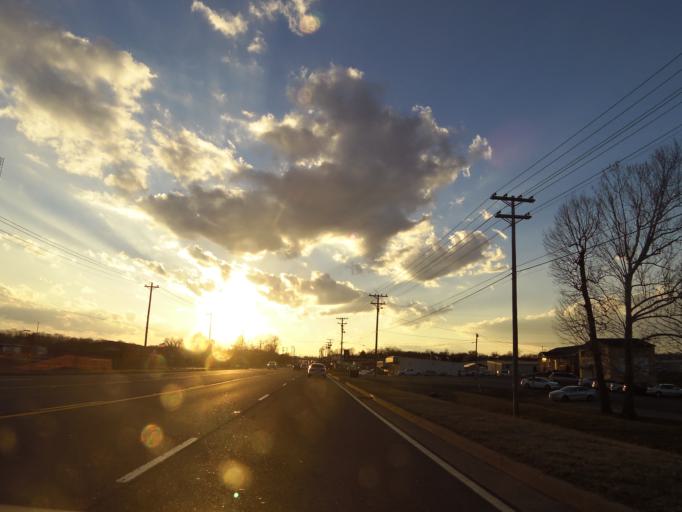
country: US
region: Tennessee
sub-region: Wilson County
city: Mount Juliet
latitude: 36.2311
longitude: -86.5070
